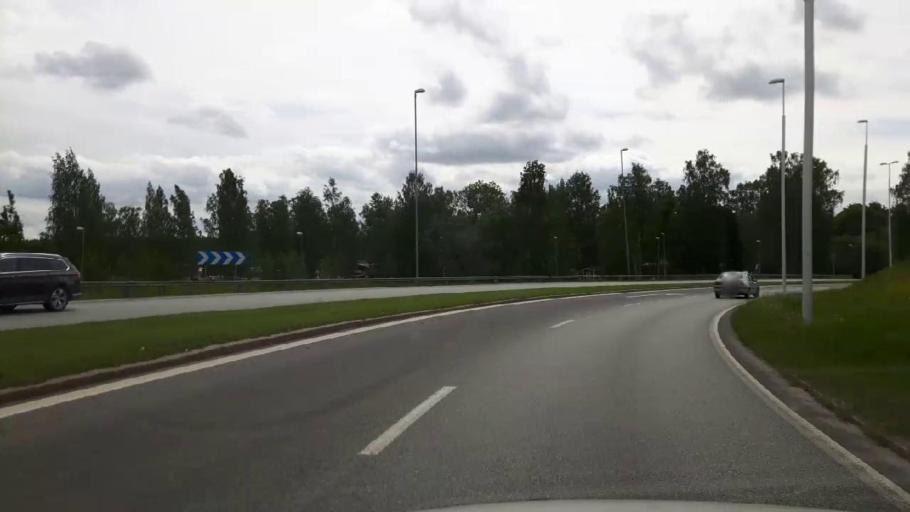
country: SE
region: Vaestmanland
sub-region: Fagersta Kommun
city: Fagersta
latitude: 59.9860
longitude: 15.8159
